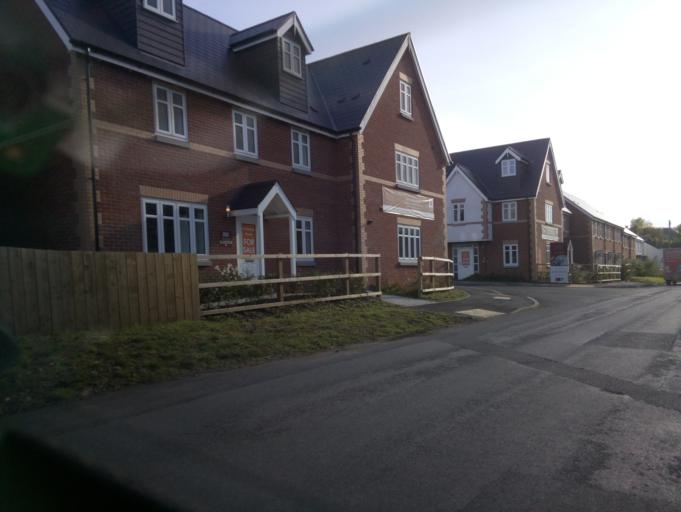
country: GB
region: Wales
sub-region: Sir Powys
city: Hay
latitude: 52.0792
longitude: -3.1231
